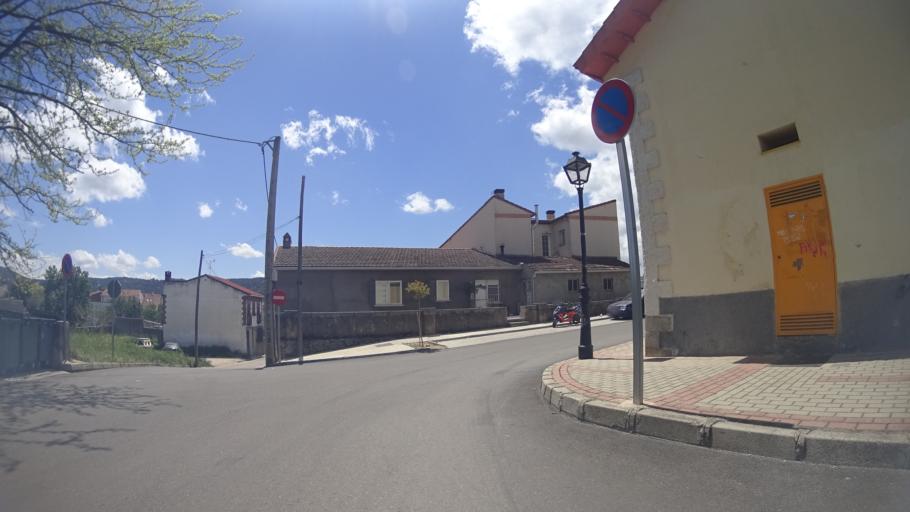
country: ES
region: Madrid
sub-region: Provincia de Madrid
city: San Martin de Valdeiglesias
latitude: 40.3653
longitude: -4.3966
